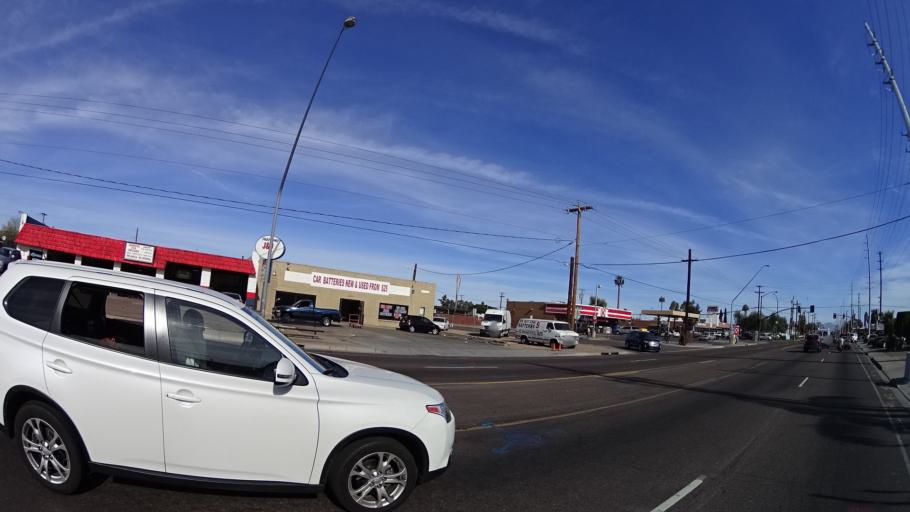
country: US
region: Arizona
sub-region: Maricopa County
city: Mesa
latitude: 33.4077
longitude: -111.8242
